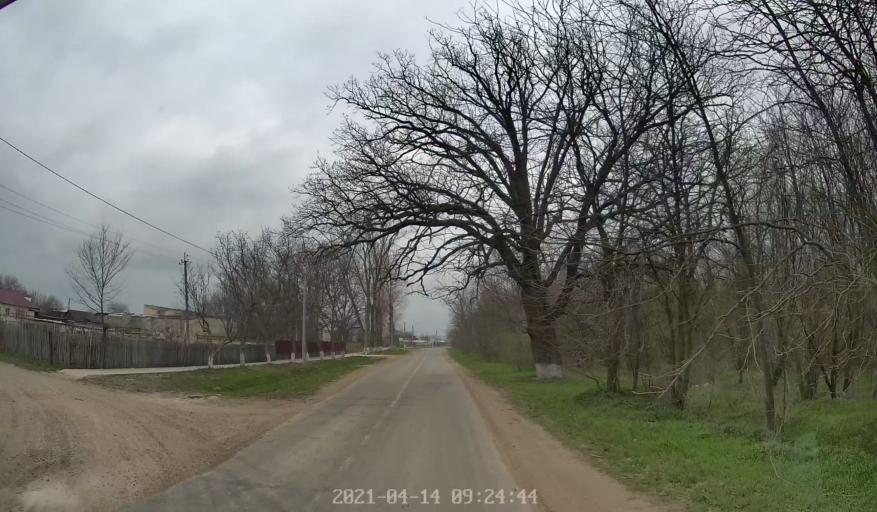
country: MD
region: Chisinau
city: Vadul lui Voda
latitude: 47.1112
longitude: 29.1138
